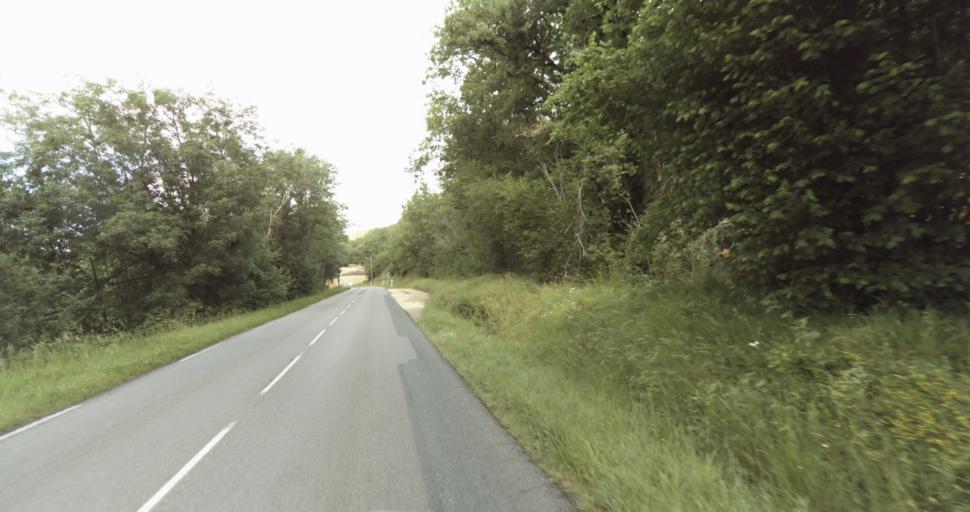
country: FR
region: Aquitaine
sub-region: Departement de la Dordogne
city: Lalinde
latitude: 44.8008
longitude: 0.7376
